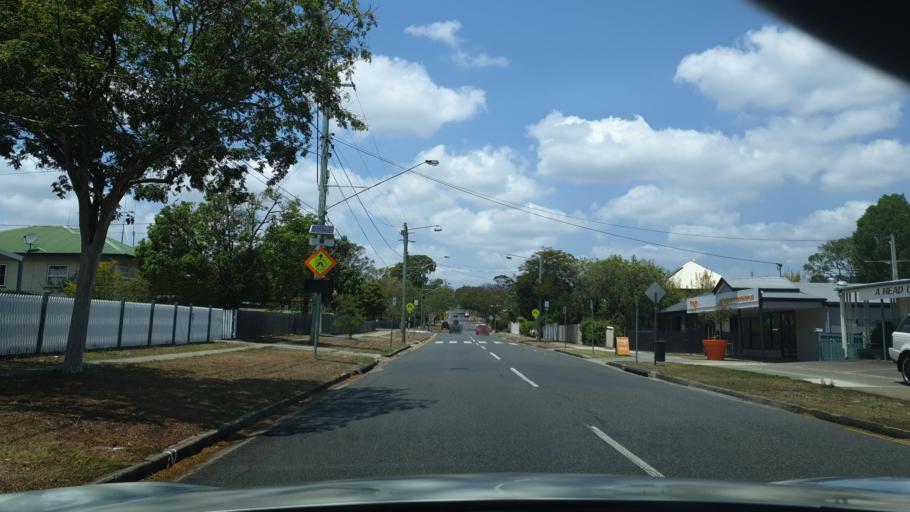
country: AU
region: Queensland
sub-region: Brisbane
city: Zillmere
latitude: -27.3611
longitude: 153.0272
